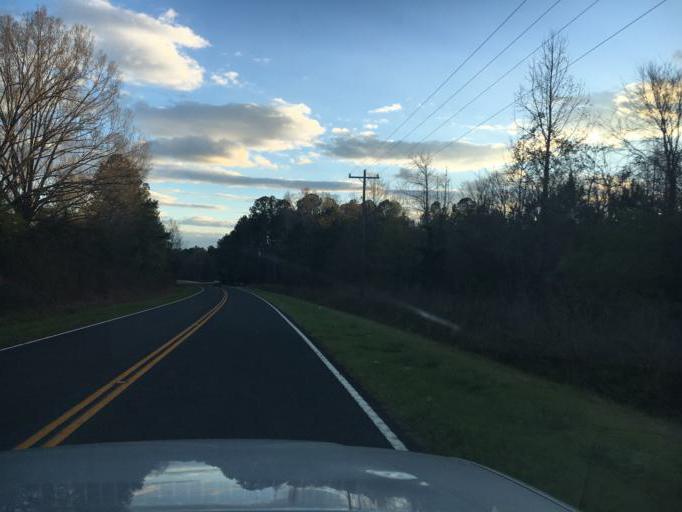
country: US
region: South Carolina
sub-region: Greenwood County
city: Greenwood
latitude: 34.1094
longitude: -82.1843
